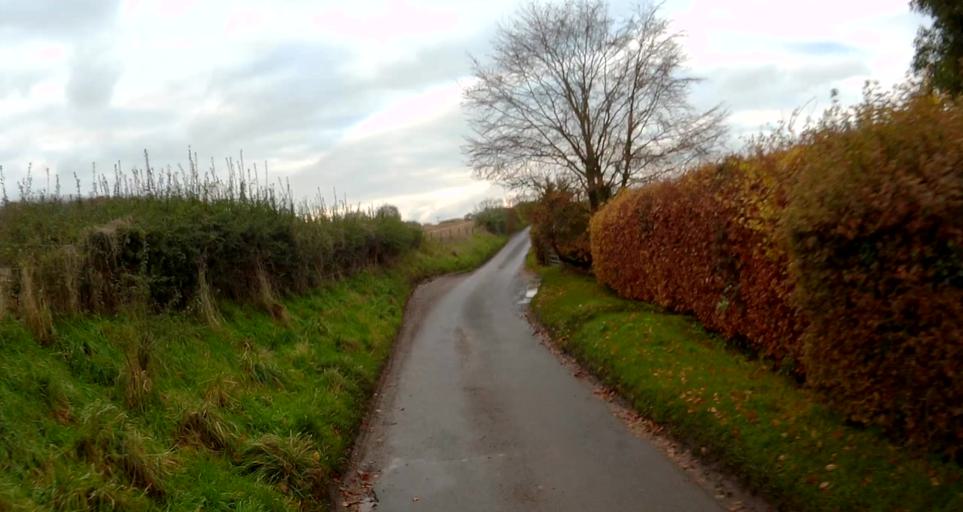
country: GB
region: England
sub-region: Hampshire
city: Long Sutton
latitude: 51.2134
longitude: -0.8844
